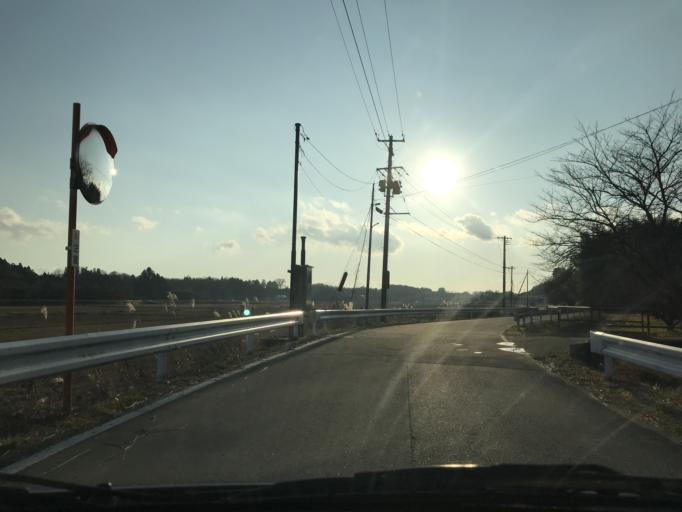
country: JP
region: Miyagi
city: Wakuya
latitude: 38.7075
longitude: 141.1275
